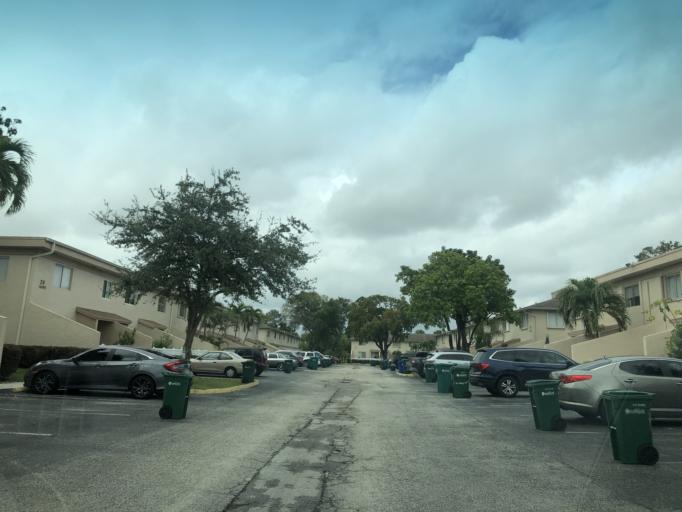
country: US
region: Florida
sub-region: Broward County
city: Margate
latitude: 26.2489
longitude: -80.2334
